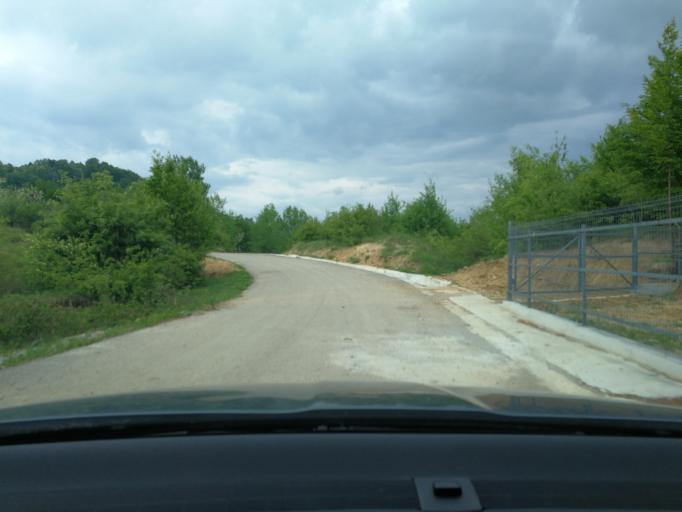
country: RO
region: Prahova
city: Cornu de Sus
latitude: 45.1731
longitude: 25.7067
